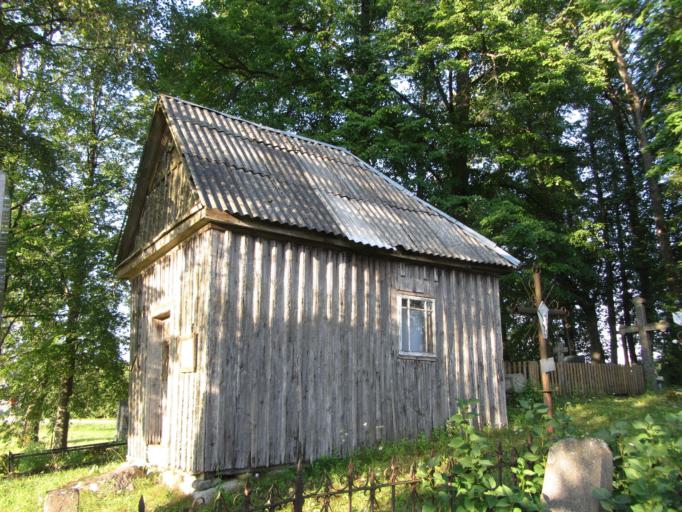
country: LT
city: Ignalina
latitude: 55.3378
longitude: 26.2757
